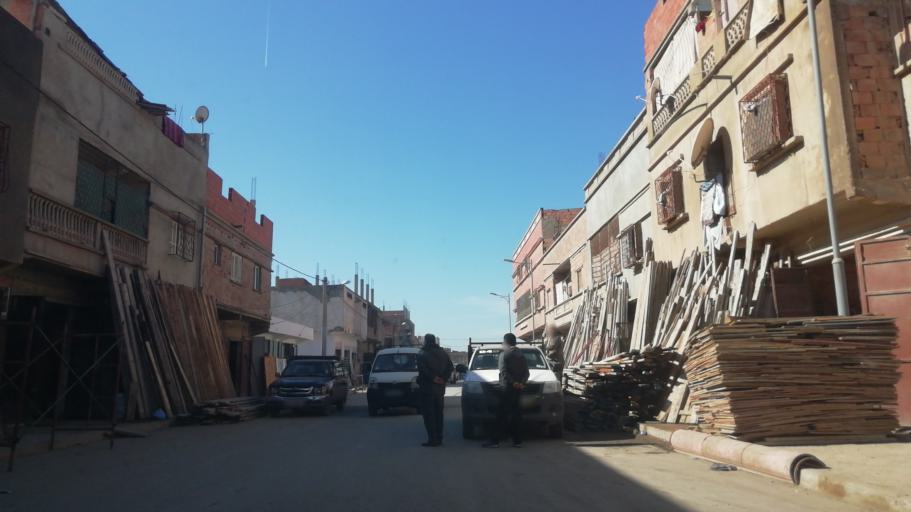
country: DZ
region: Oran
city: Es Senia
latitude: 35.6463
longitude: -0.5726
